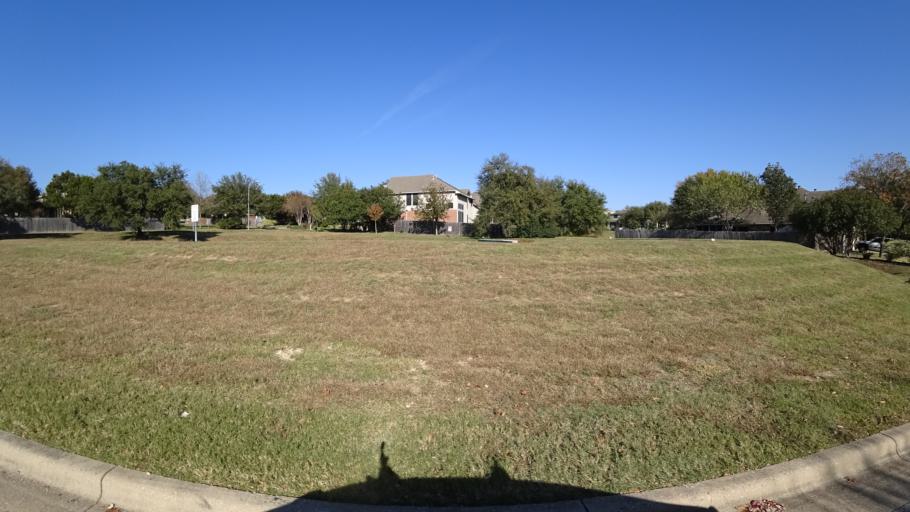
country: US
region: Texas
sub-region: Travis County
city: Barton Creek
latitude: 30.2258
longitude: -97.8772
